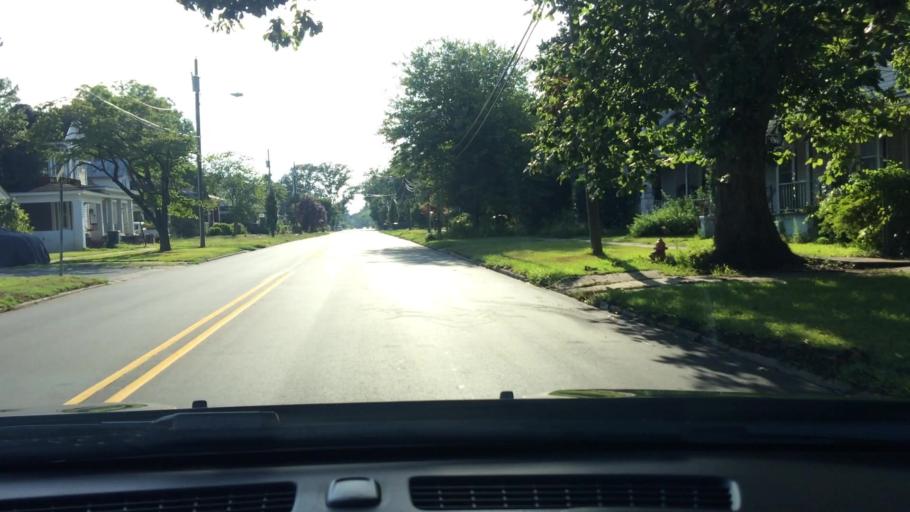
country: US
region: North Carolina
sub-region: Pitt County
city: Ayden
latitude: 35.4708
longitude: -77.4118
